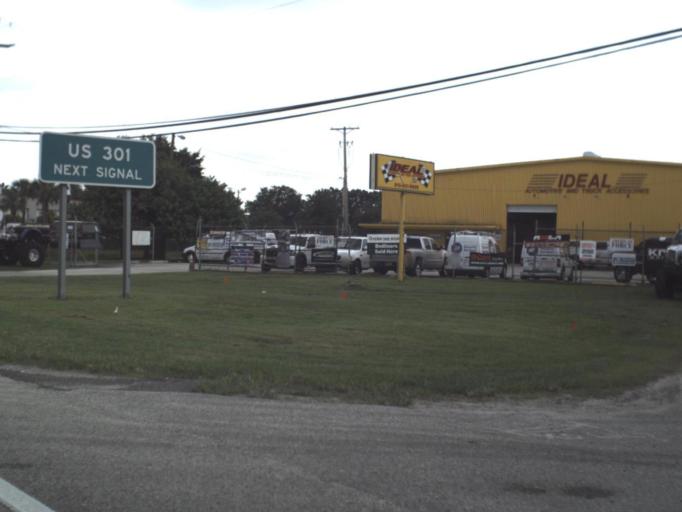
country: US
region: Florida
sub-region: Hillsborough County
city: Palm River-Clair Mel
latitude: 27.9502
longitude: -82.3611
